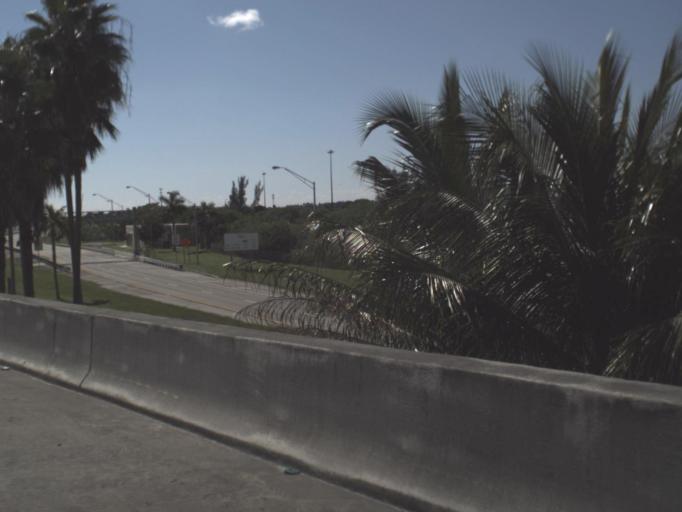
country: US
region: Florida
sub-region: Miami-Dade County
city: Richmond Heights
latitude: 25.6273
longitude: -80.3799
